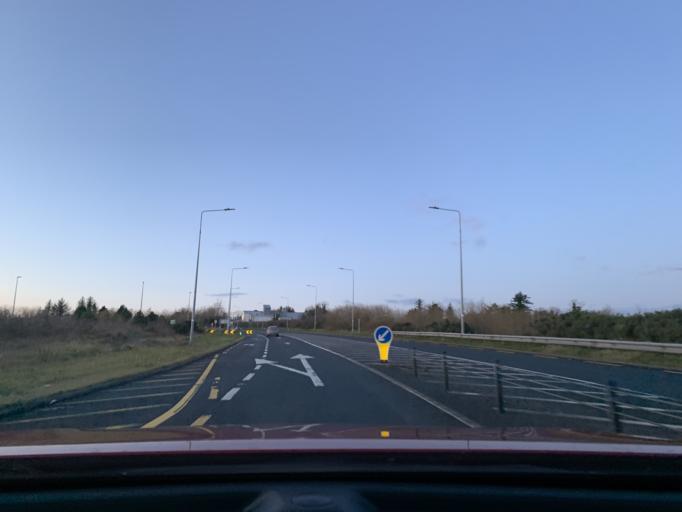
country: IE
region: Connaught
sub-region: County Leitrim
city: Carrick-on-Shannon
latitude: 53.8801
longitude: -7.9334
